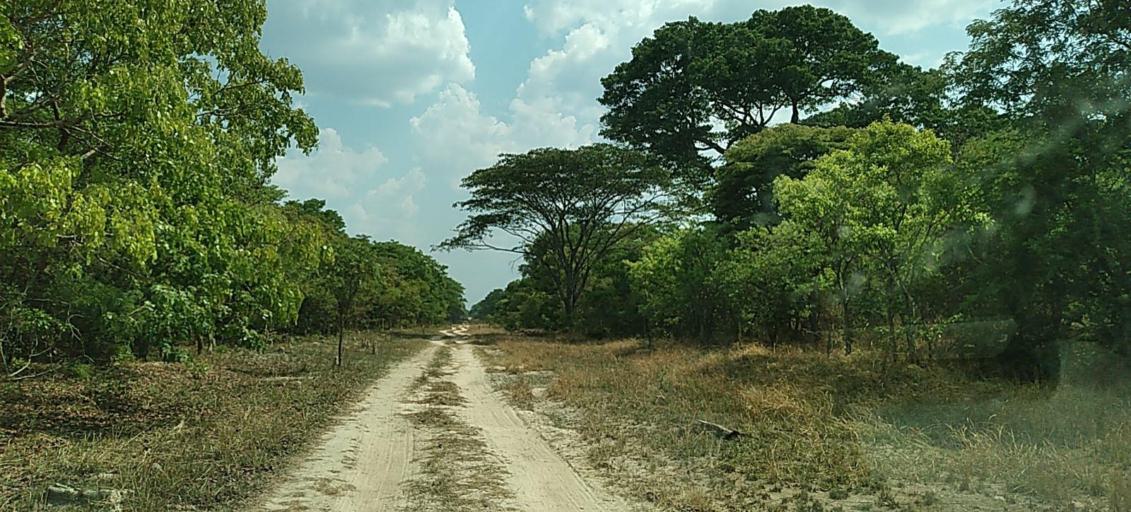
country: ZM
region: Copperbelt
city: Mpongwe
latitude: -13.8352
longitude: 27.9380
